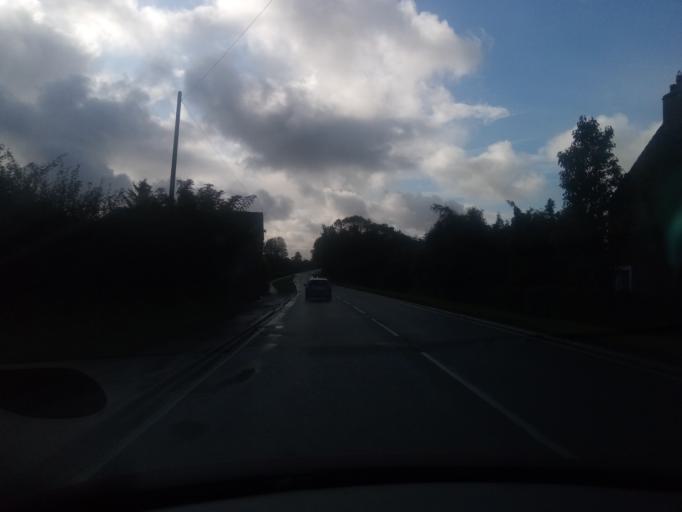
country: GB
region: England
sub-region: Cumbria
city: Carlisle
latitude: 54.9465
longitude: -2.9434
